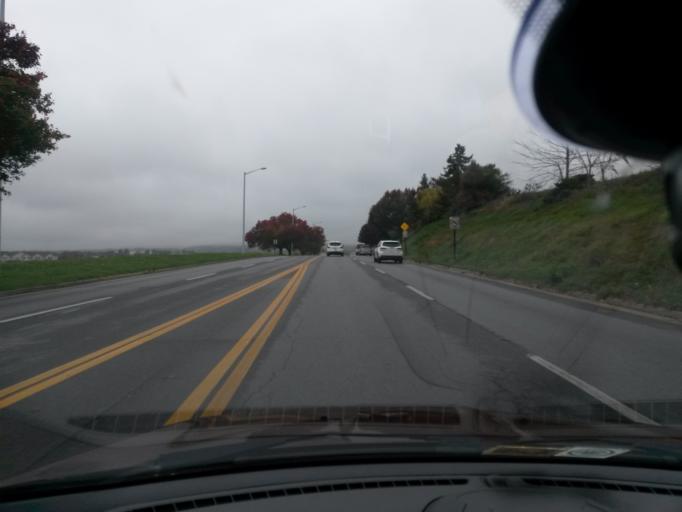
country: US
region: Virginia
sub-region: Roanoke County
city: Hollins
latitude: 37.3092
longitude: -79.9631
